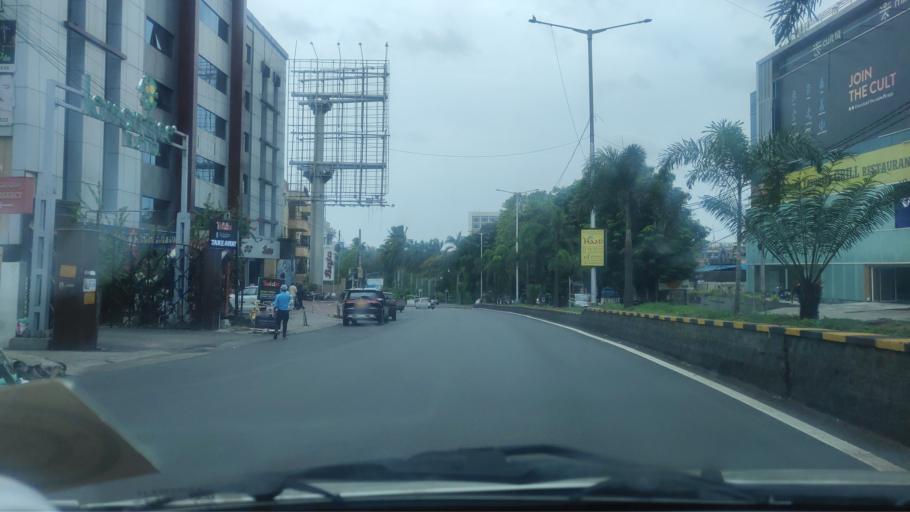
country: IN
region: Telangana
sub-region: Hyderabad
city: Hyderabad
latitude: 17.4125
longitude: 78.4499
